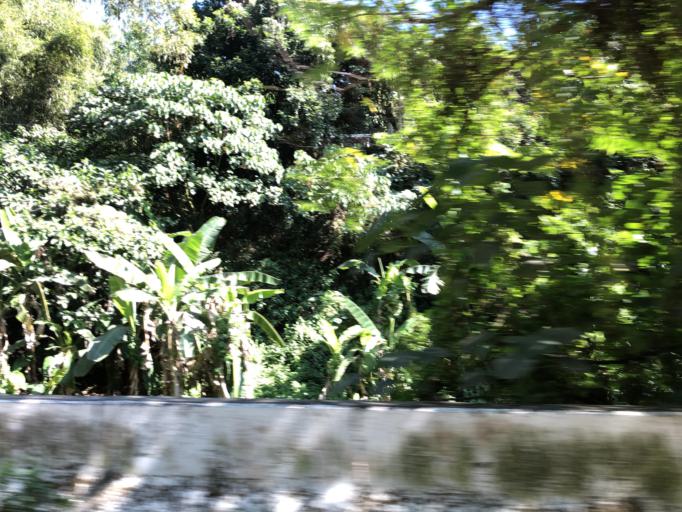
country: TW
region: Taiwan
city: Yujing
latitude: 23.0554
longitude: 120.3790
